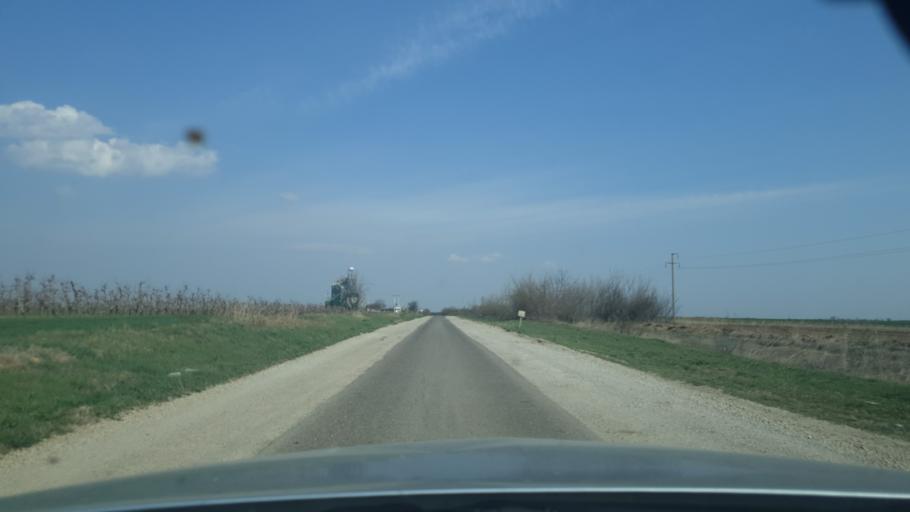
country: RS
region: Autonomna Pokrajina Vojvodina
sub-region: Sremski Okrug
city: Irig
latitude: 45.1021
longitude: 19.8993
